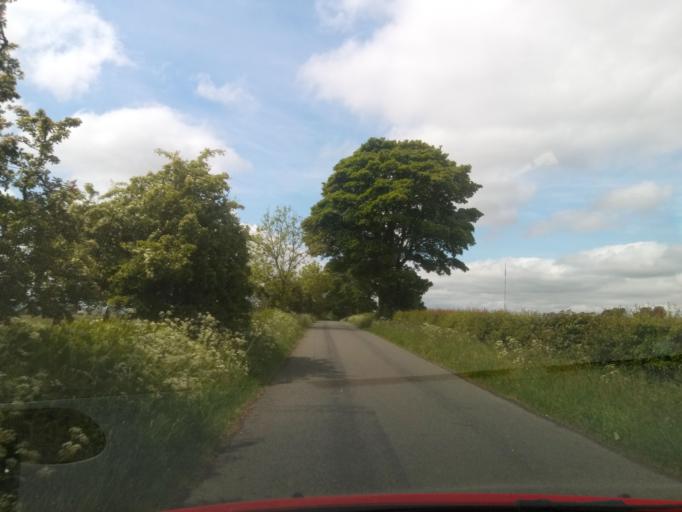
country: GB
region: Scotland
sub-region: The Scottish Borders
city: Selkirk
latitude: 55.5136
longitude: -2.8062
